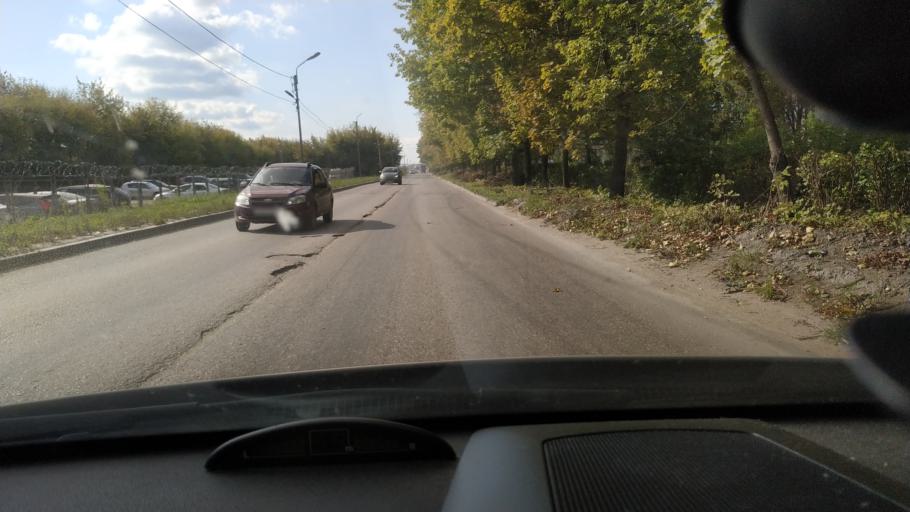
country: RU
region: Rjazan
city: Ryazan'
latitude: 54.6503
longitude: 39.6515
